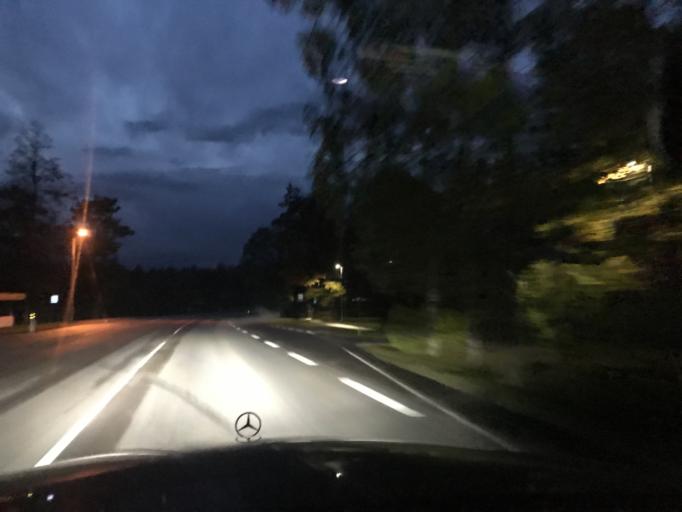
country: EE
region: Valgamaa
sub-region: Torva linn
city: Torva
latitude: 58.0136
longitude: 25.8832
